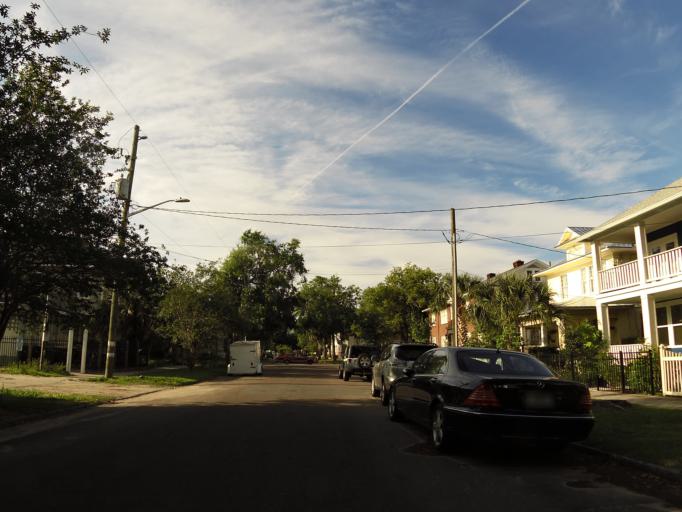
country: US
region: Florida
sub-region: Duval County
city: Jacksonville
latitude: 30.3479
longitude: -81.6553
